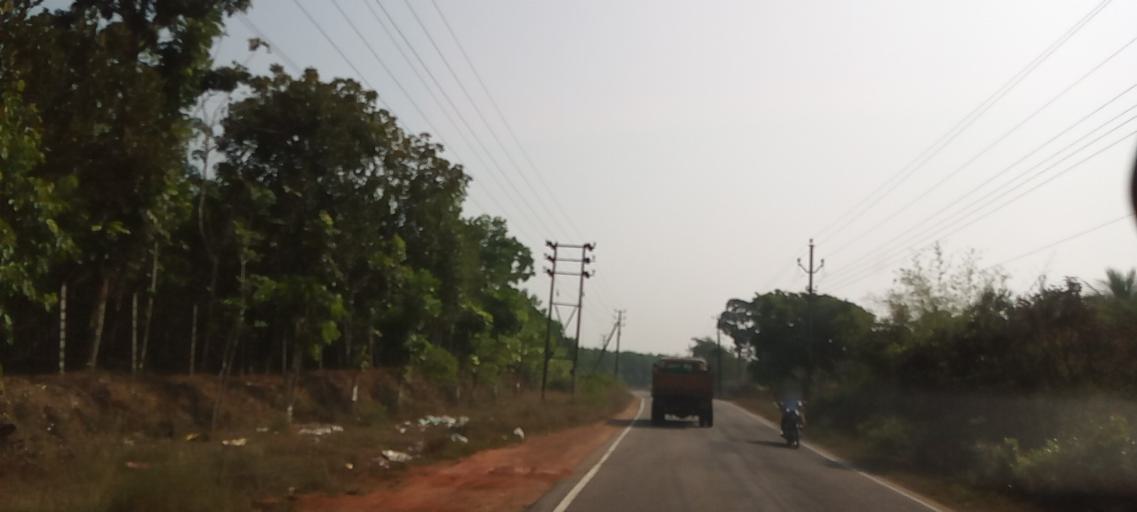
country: IN
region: Karnataka
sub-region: Udupi
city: Coondapoor
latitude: 13.5160
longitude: 74.7561
